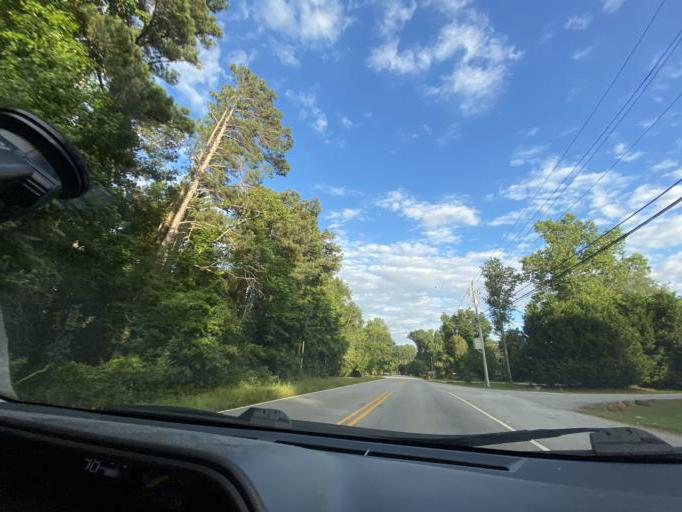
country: US
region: Georgia
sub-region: Fayette County
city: Tyrone
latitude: 33.4372
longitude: -84.6529
